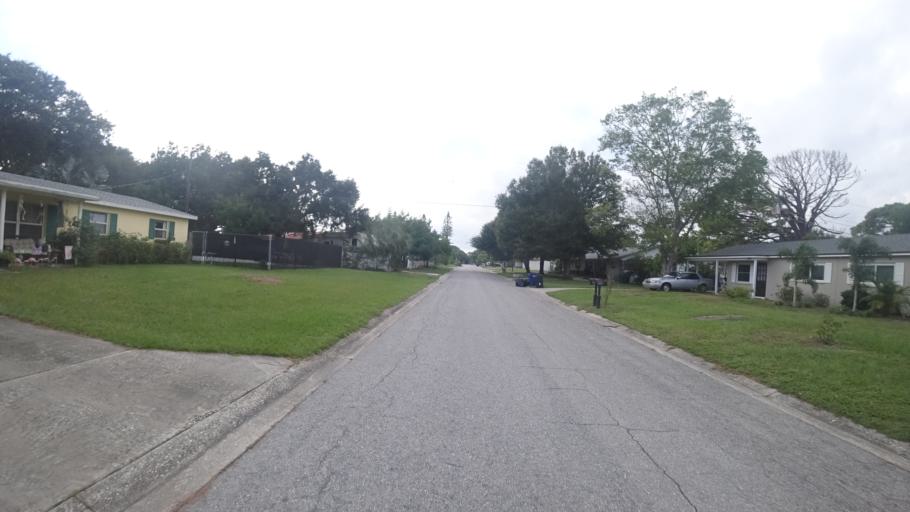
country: US
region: Florida
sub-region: Manatee County
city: South Bradenton
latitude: 27.4518
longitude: -82.5802
